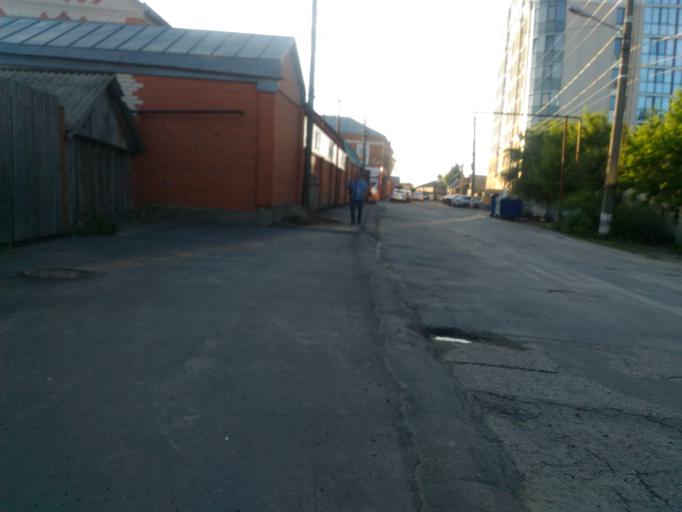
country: RU
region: Ulyanovsk
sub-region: Ulyanovskiy Rayon
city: Ulyanovsk
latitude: 54.3167
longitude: 48.3798
